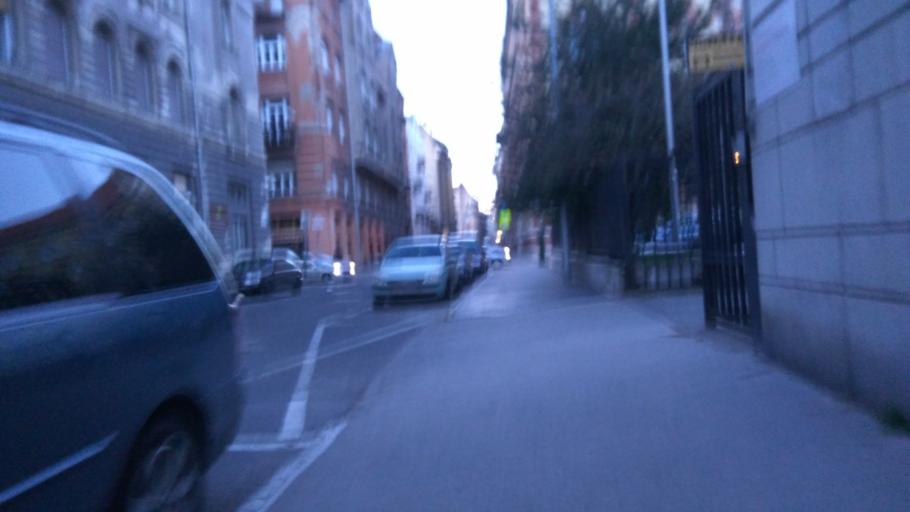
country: HU
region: Budapest
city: Budapest VIII. keruelet
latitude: 47.4908
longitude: 19.0738
